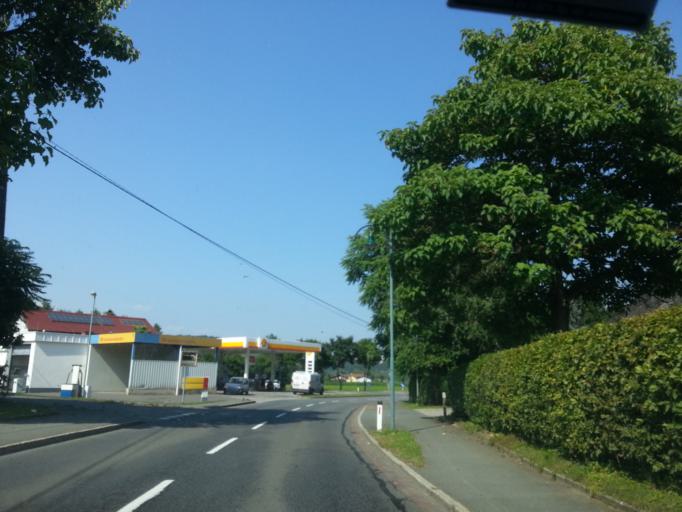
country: AT
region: Styria
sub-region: Politischer Bezirk Leibnitz
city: Heimschuh
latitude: 46.7637
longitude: 15.4939
